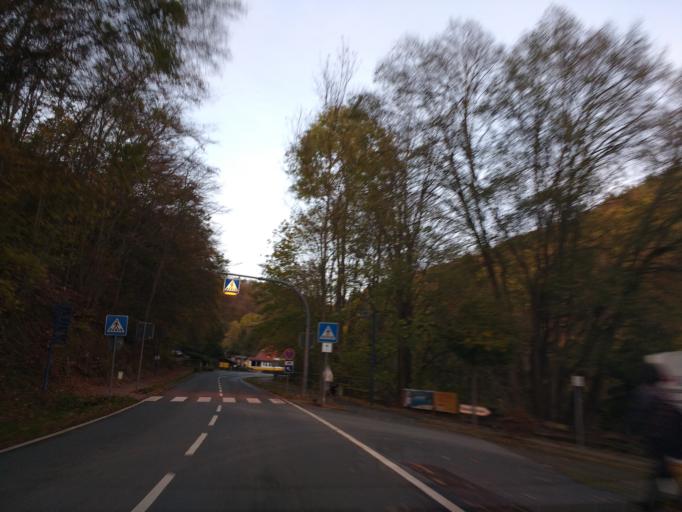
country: DE
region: Hesse
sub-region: Regierungsbezirk Kassel
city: Waldeck
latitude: 51.2019
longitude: 9.0492
